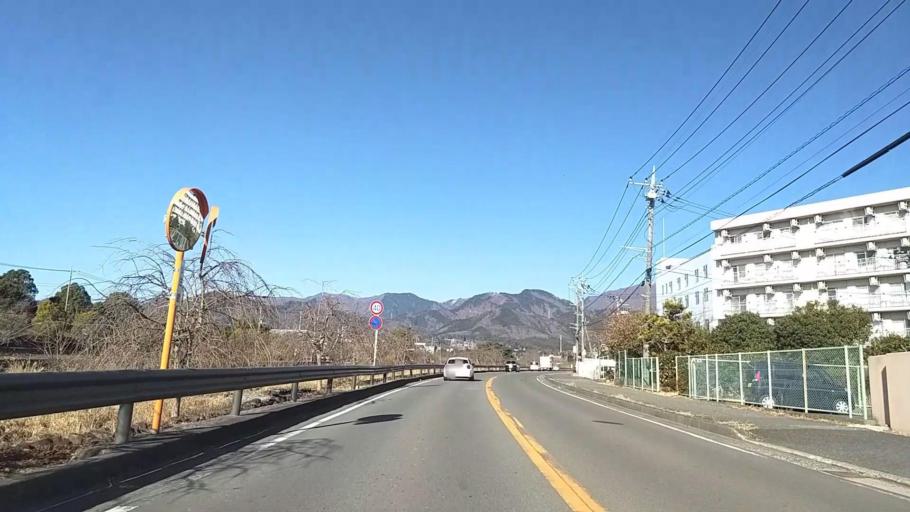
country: JP
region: Kanagawa
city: Hadano
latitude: 35.3882
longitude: 139.1880
